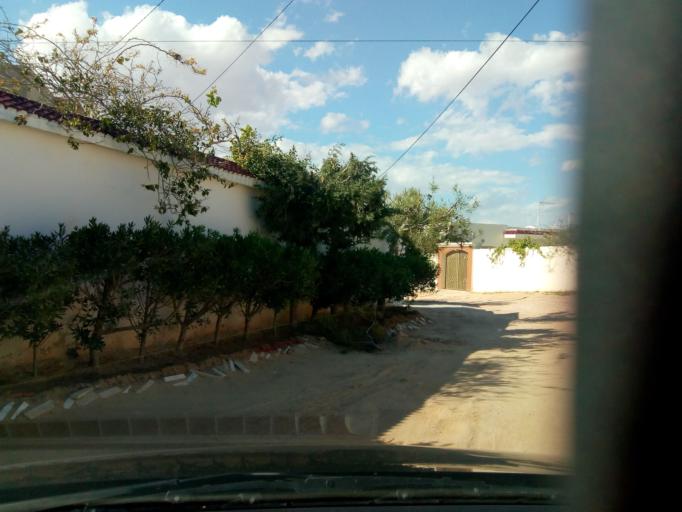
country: TN
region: Safaqis
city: Sfax
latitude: 34.7304
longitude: 10.6023
